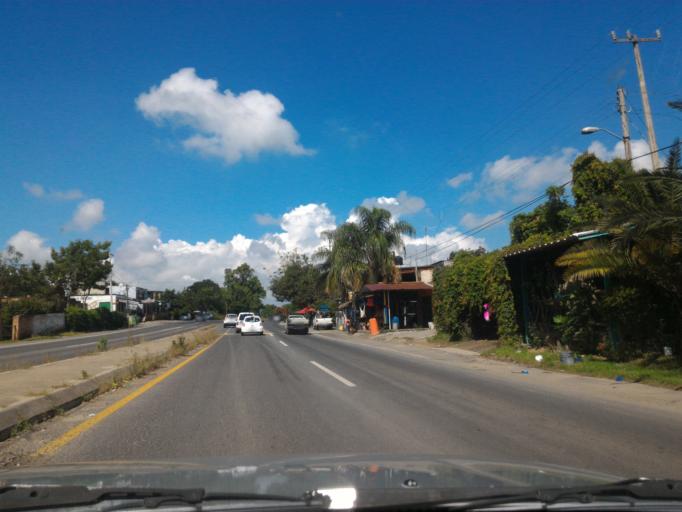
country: MX
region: Jalisco
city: Arenal
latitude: 20.7479
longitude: -103.6454
